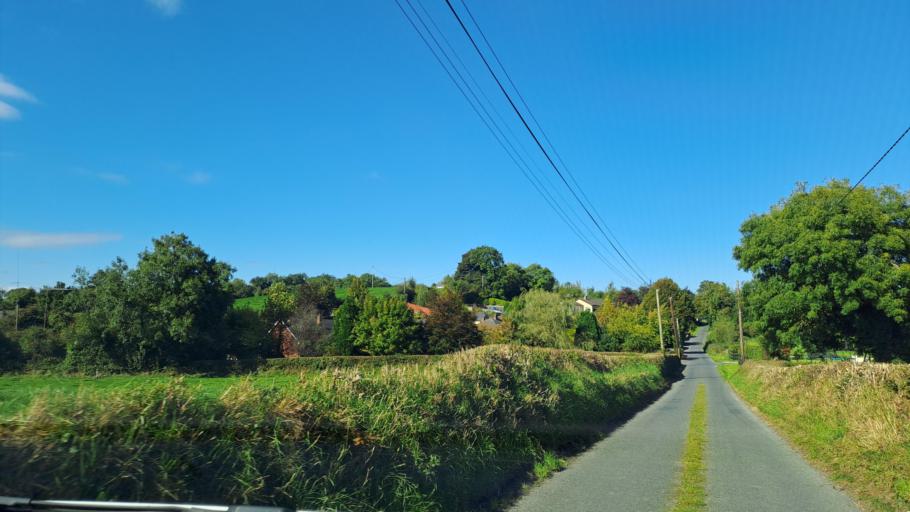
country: IE
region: Ulster
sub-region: County Monaghan
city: Carrickmacross
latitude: 53.9885
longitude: -6.7502
